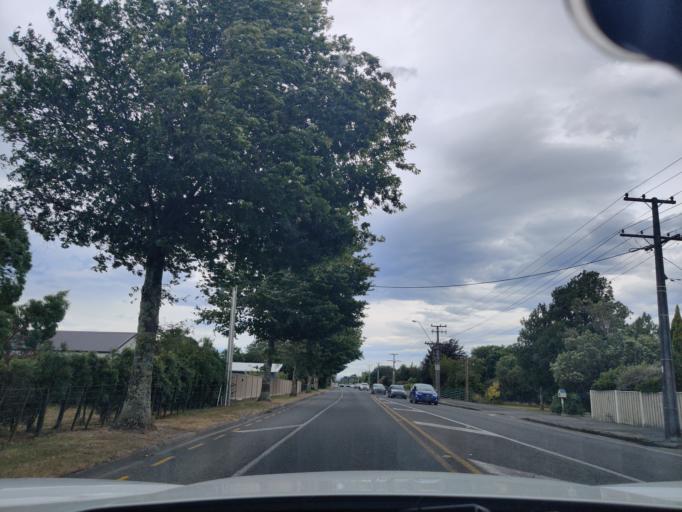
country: NZ
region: Wellington
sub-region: Masterton District
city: Masterton
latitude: -41.0436
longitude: 175.5079
